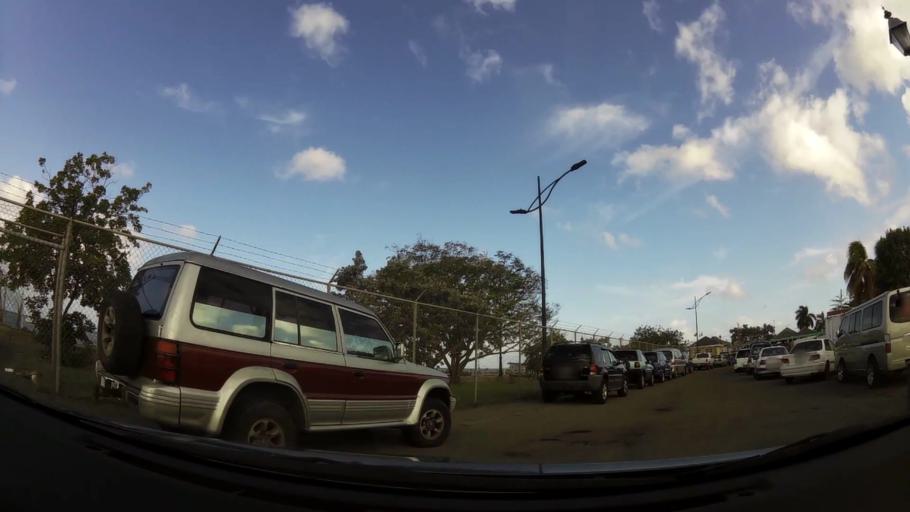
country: KN
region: Saint Paul Charlestown
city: Charlestown
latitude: 17.1377
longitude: -62.6299
